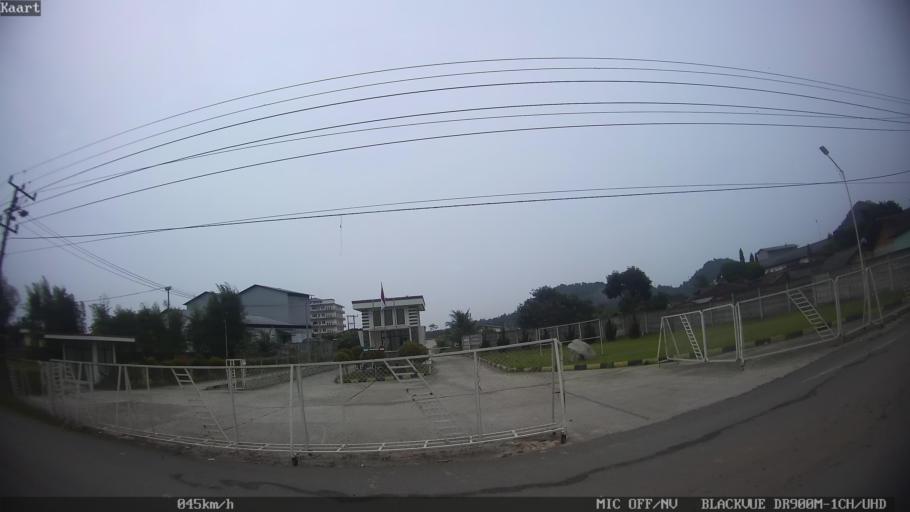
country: ID
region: Lampung
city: Panjang
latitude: -5.4173
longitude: 105.3430
